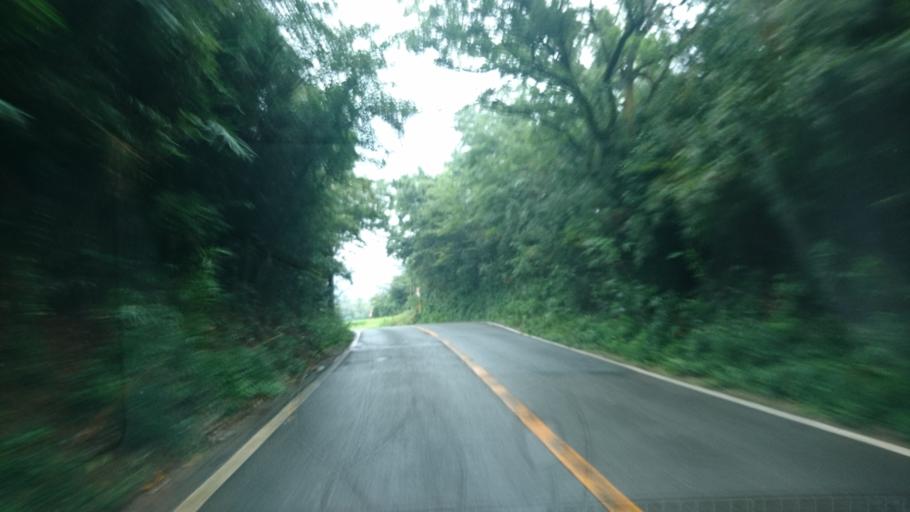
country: JP
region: Chiba
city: Kimitsu
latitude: 35.2857
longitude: 139.9807
